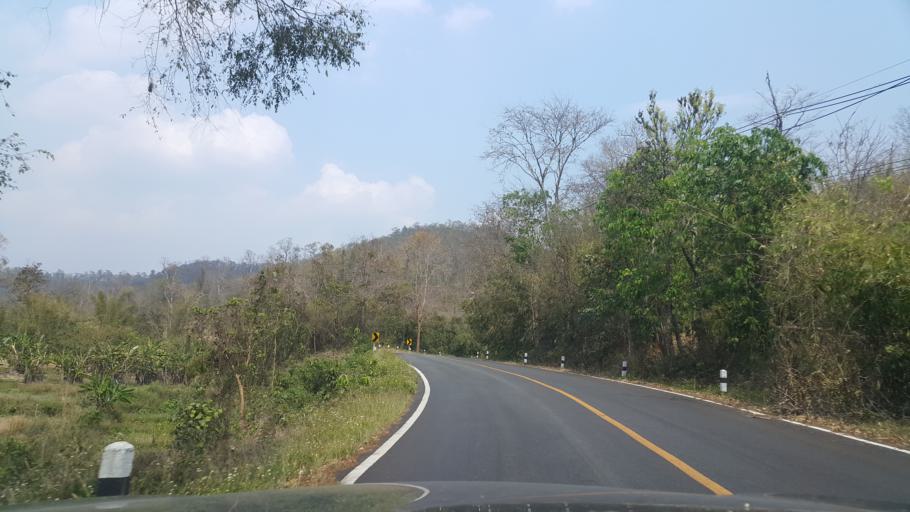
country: TH
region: Lamphun
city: Thung Hua Chang
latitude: 17.9052
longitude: 99.1383
